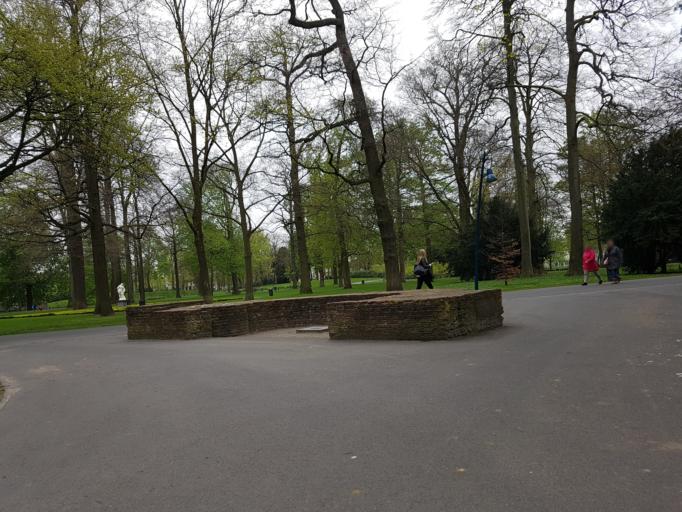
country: NL
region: North Brabant
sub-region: Gemeente Breda
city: Breda
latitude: 51.5906
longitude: 4.7784
